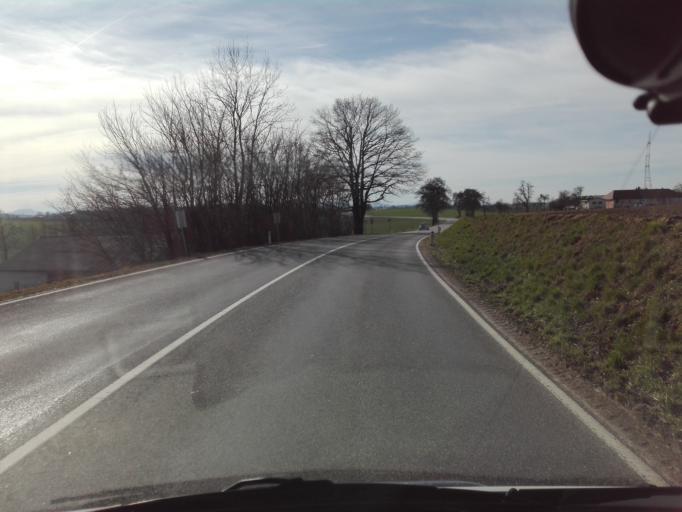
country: AT
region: Lower Austria
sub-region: Politischer Bezirk Amstetten
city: Strengberg
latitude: 48.1571
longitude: 14.7094
